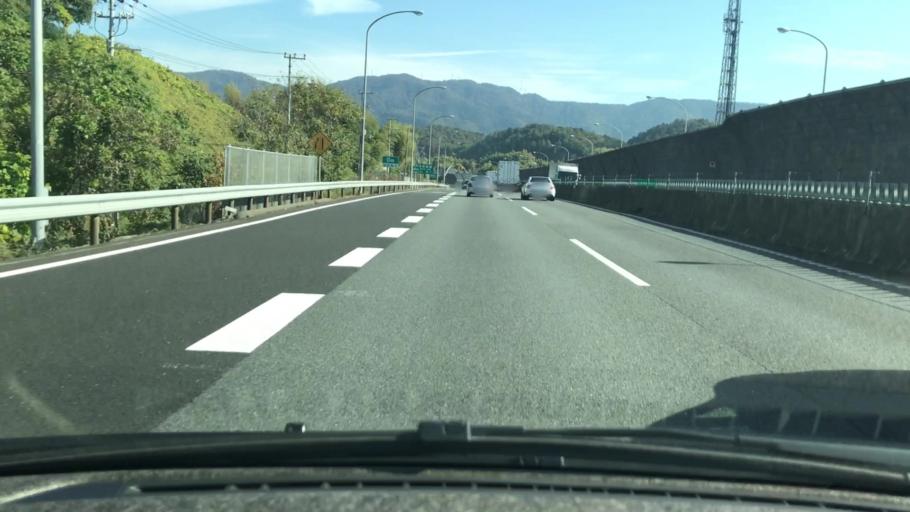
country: JP
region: Kyoto
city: Uji
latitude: 34.9551
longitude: 135.7905
